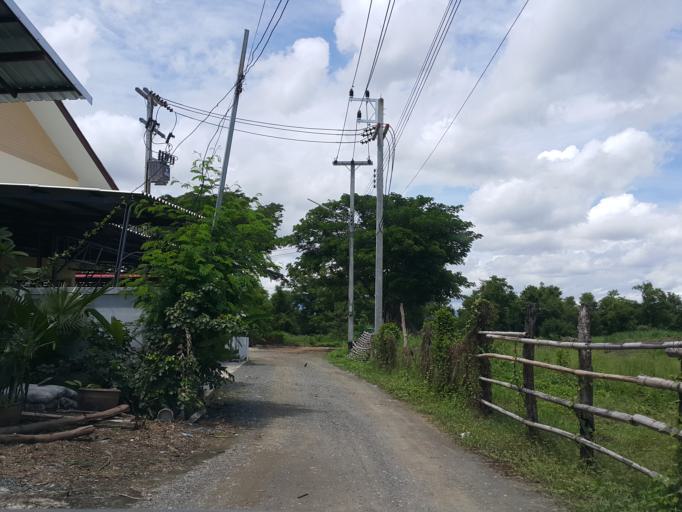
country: TH
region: Chiang Mai
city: San Kamphaeng
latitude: 18.7620
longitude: 99.1024
